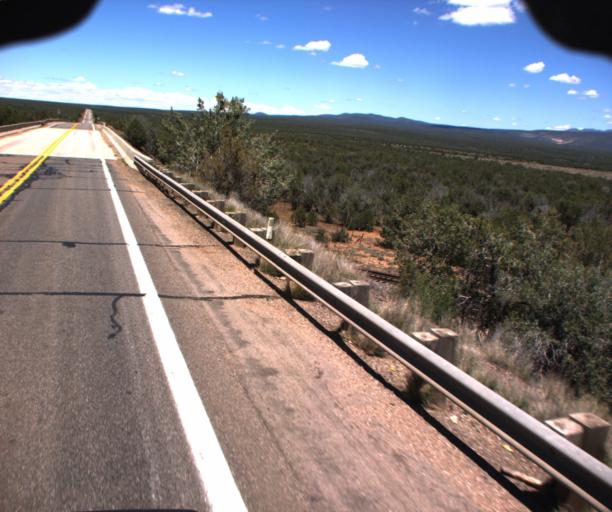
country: US
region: Arizona
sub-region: Yavapai County
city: Paulden
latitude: 35.0101
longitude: -112.3907
